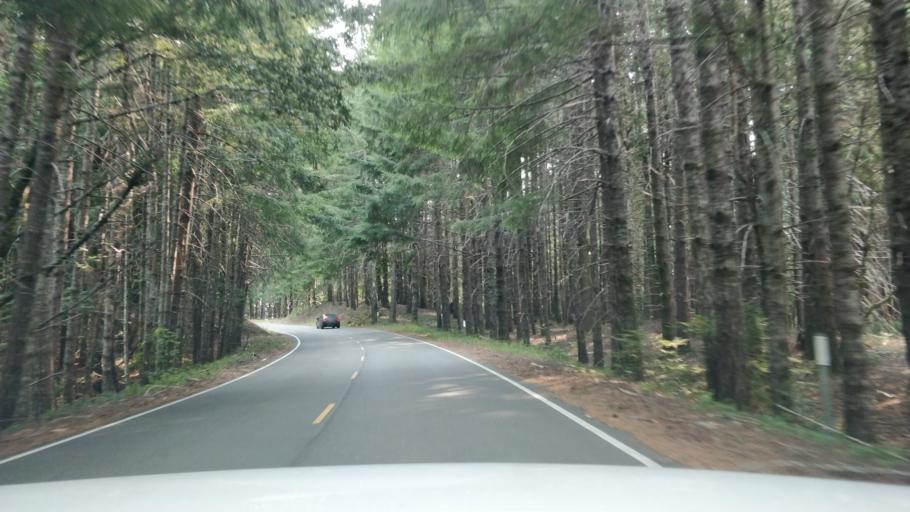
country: US
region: California
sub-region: Humboldt County
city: Westhaven-Moonstone
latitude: 41.2103
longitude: -123.9565
